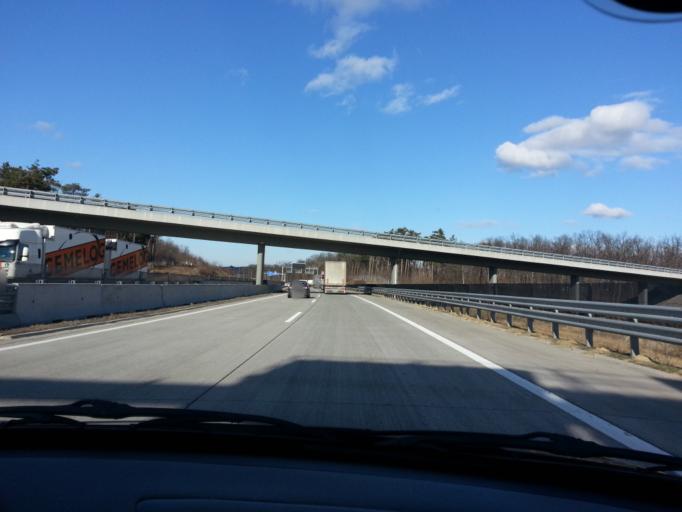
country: HU
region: Pest
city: Szada
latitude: 47.6014
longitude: 19.3211
